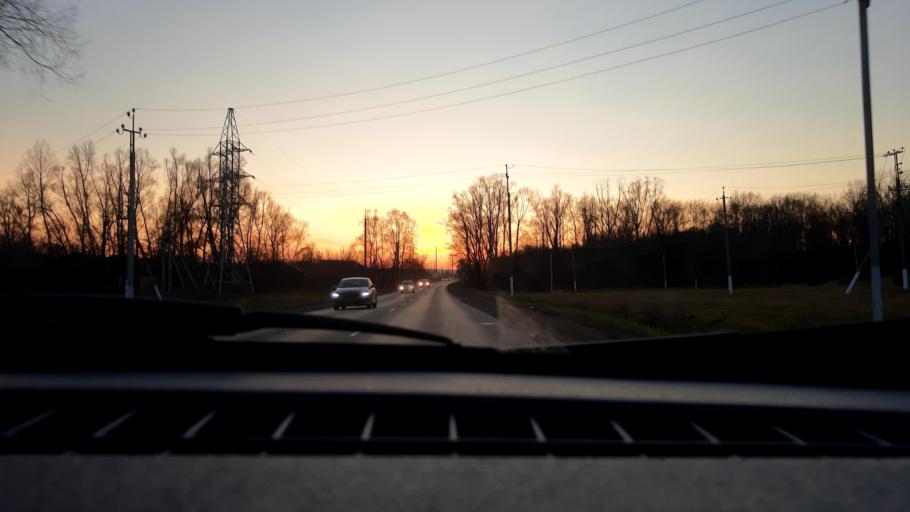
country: RU
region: Bashkortostan
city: Mikhaylovka
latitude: 54.8055
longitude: 55.8742
